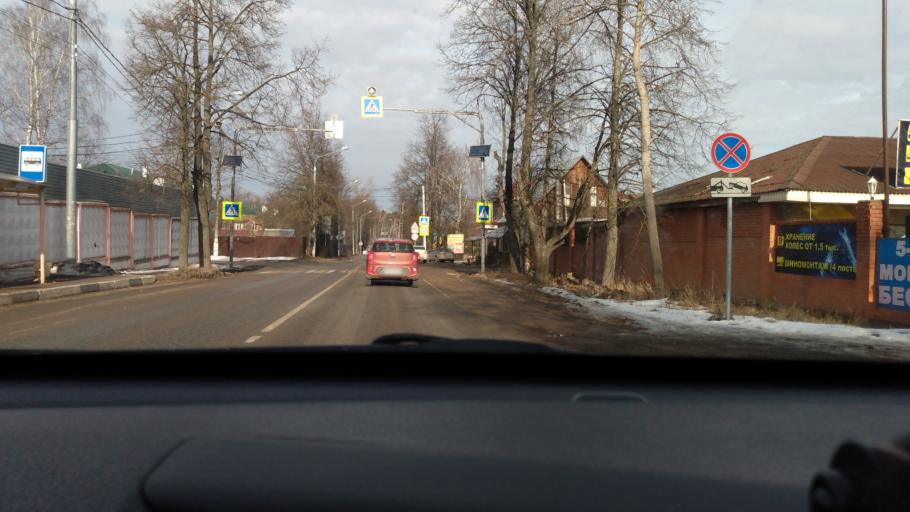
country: RU
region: Moskovskaya
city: Nakhabino
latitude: 55.8639
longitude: 37.1855
